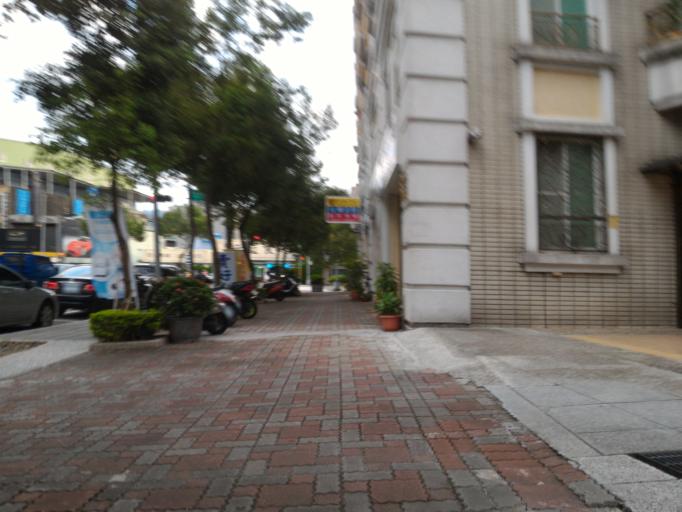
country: TW
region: Taiwan
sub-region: Taoyuan
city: Taoyuan
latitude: 24.9445
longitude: 121.3806
